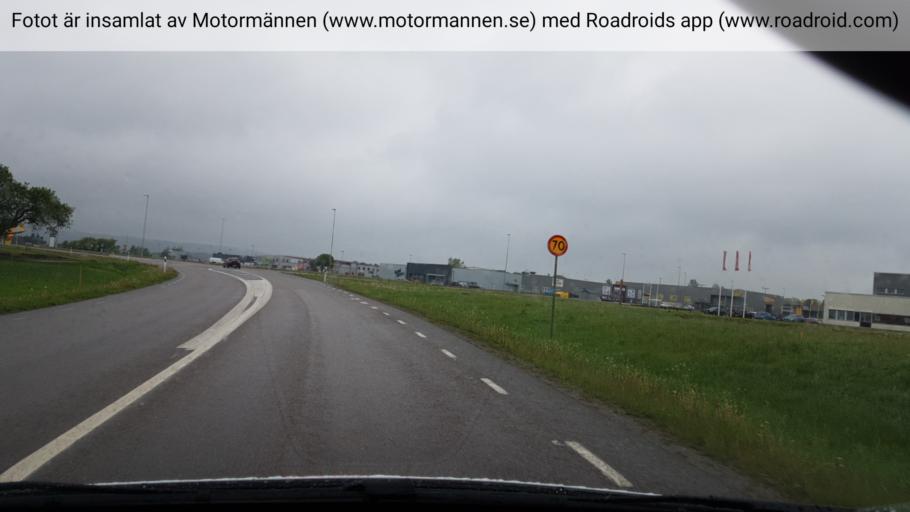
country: SE
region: Vaestra Goetaland
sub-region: Falkopings Kommun
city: Falkoeping
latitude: 58.1420
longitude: 13.5592
